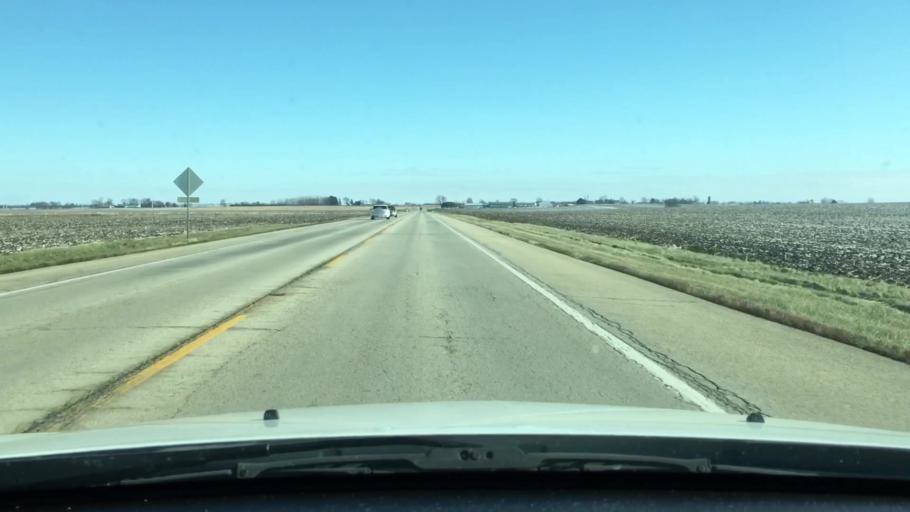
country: US
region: Illinois
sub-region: Ogle County
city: Hillcrest
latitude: 42.0077
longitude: -88.9597
